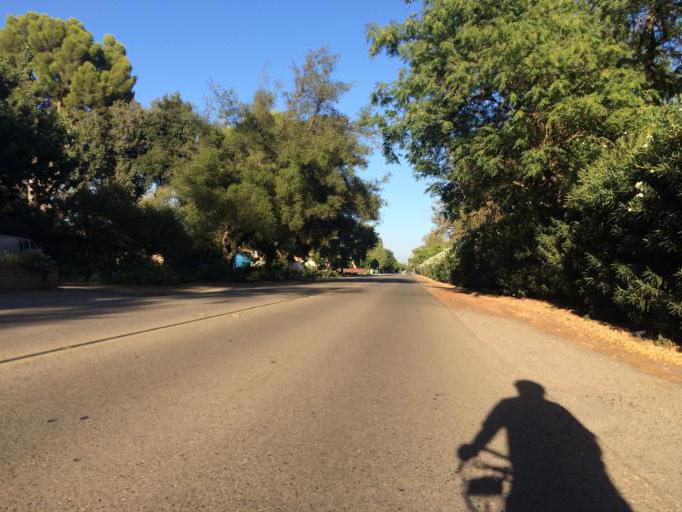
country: US
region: California
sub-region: Fresno County
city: Sunnyside
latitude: 36.7291
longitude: -119.6922
